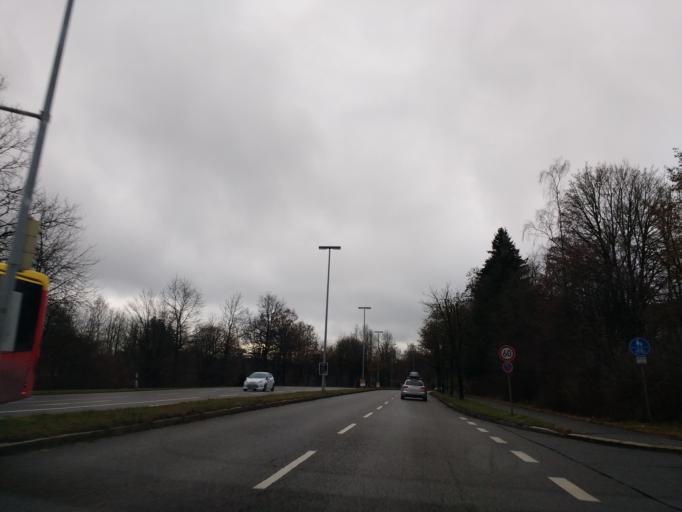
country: DE
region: Bavaria
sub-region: Swabia
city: Kempten (Allgaeu)
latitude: 47.7181
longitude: 10.3304
